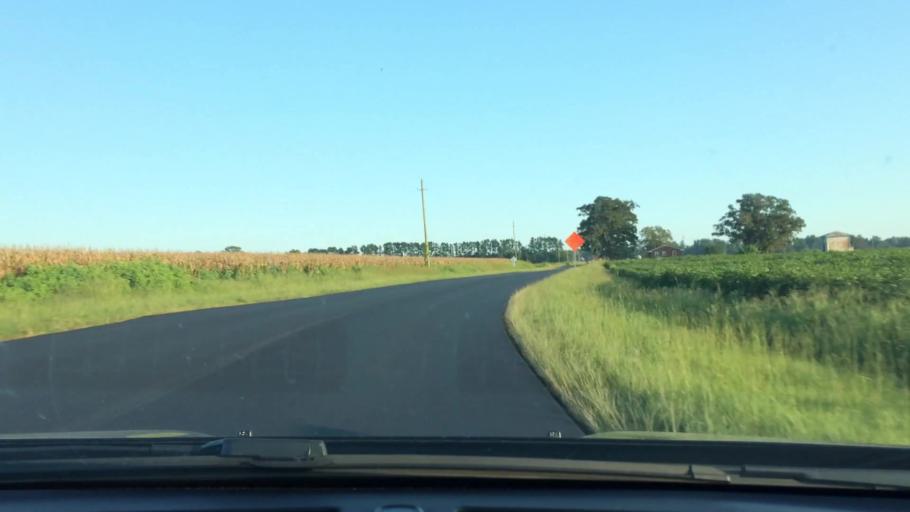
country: US
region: North Carolina
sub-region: Pitt County
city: Ayden
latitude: 35.4421
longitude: -77.4537
